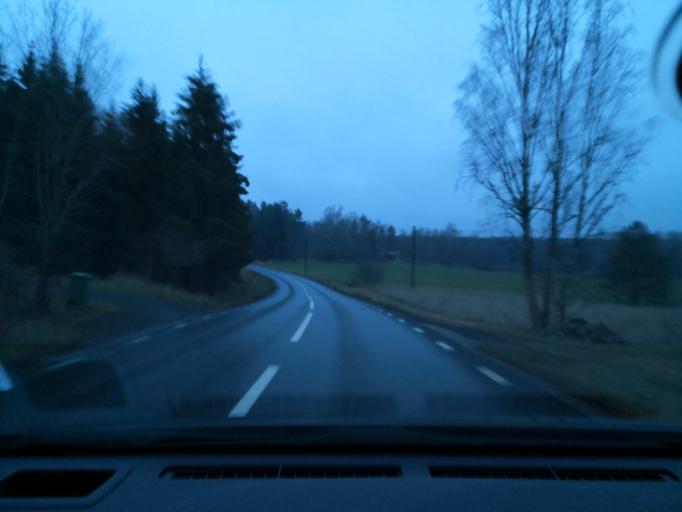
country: SE
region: Soedermanland
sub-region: Eskilstuna Kommun
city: Skogstorp
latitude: 59.2354
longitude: 16.3329
